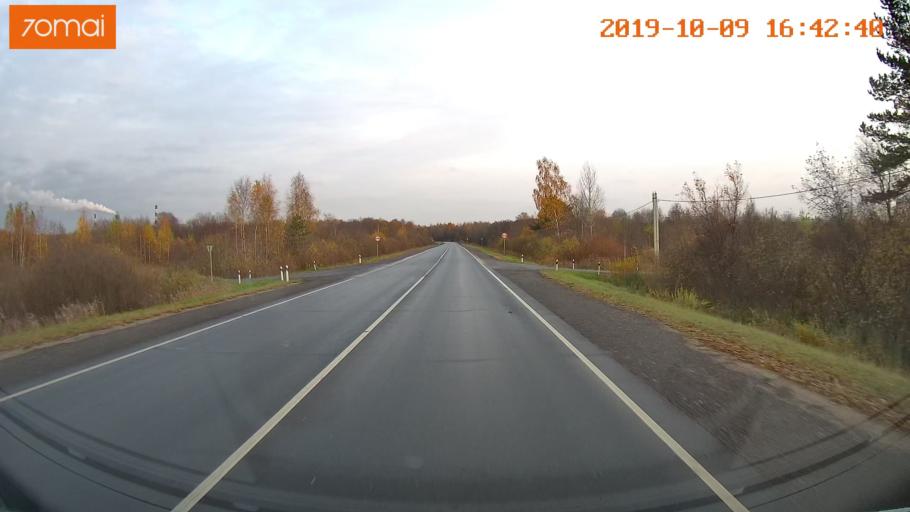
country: RU
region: Kostroma
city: Volgorechensk
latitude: 57.4597
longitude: 41.1050
